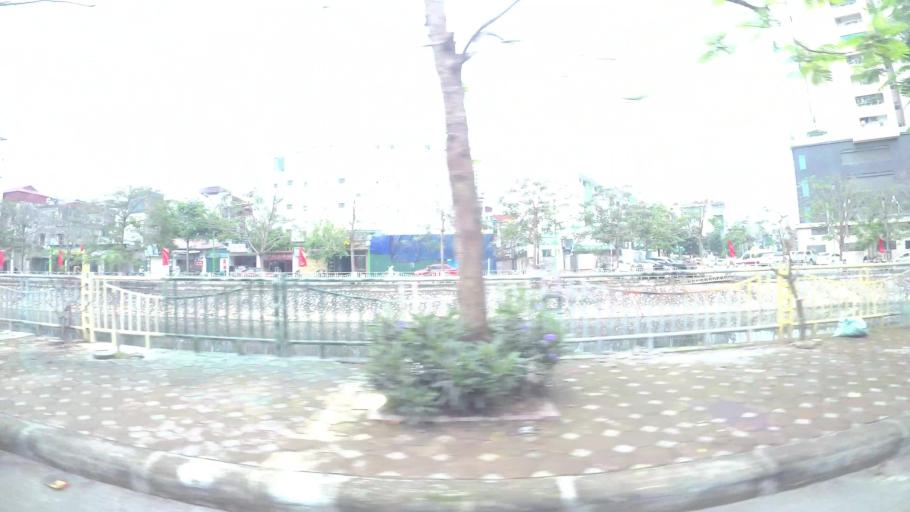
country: VN
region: Ha Noi
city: Van Dien
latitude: 20.9789
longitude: 105.8458
